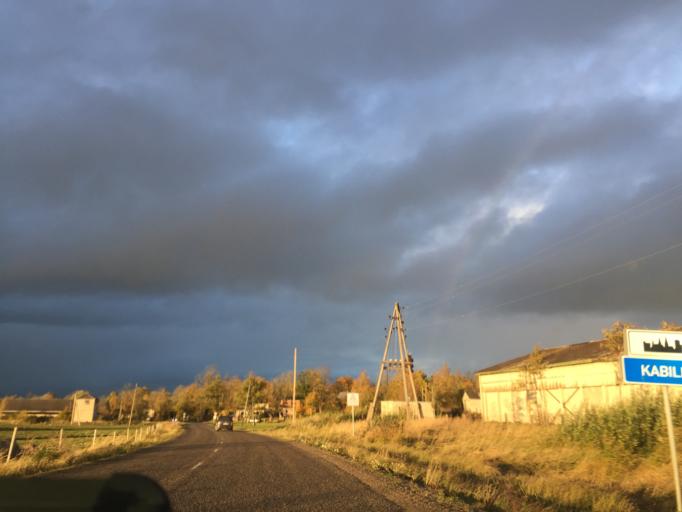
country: LV
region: Talsu Rajons
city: Sabile
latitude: 56.9462
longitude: 22.3994
